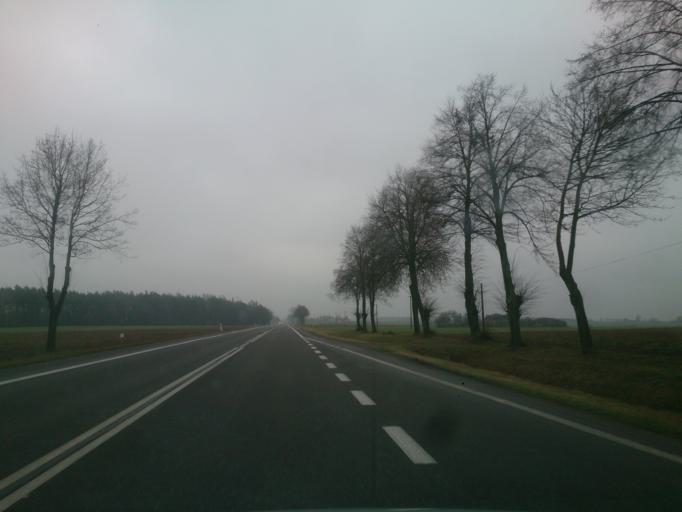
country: PL
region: Masovian Voivodeship
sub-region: Powiat plocki
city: Starozreby
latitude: 52.6640
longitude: 20.0754
